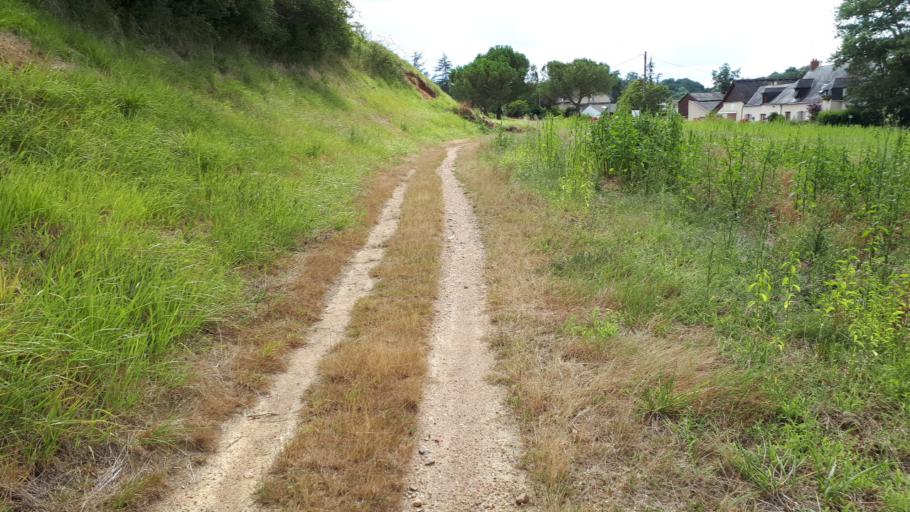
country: FR
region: Pays de la Loire
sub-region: Departement de Maine-et-Loire
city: Rochefort-sur-Loire
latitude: 47.3301
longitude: -0.6880
